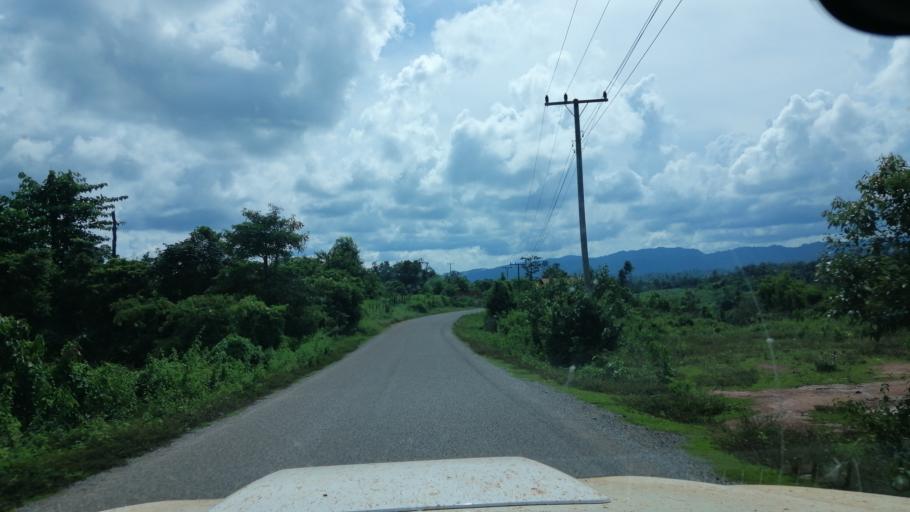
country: TH
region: Nan
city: Mae Charim
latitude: 18.3871
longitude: 101.1578
